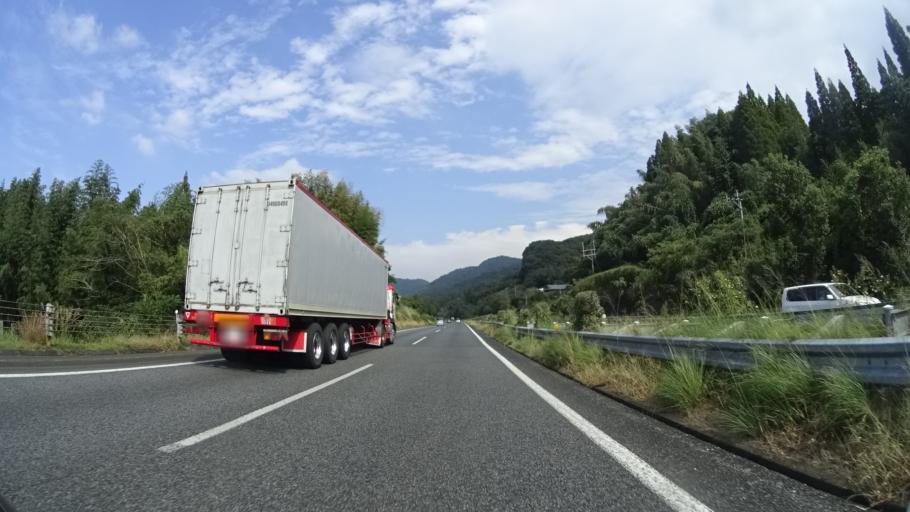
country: JP
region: Kumamoto
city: Matsubase
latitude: 32.5962
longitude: 130.7178
